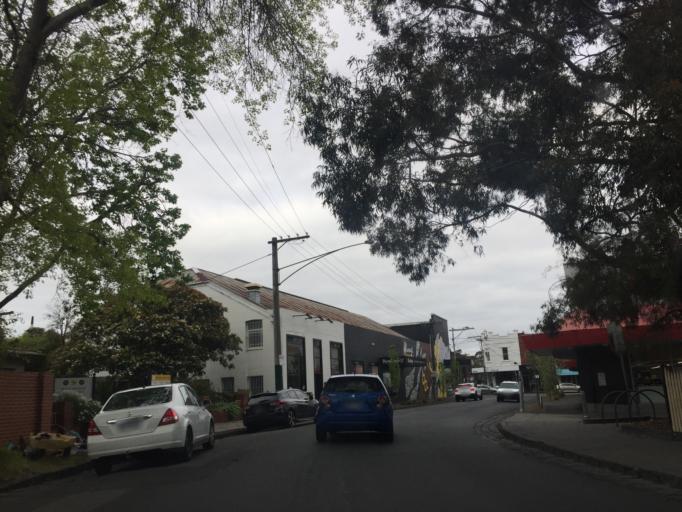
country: AU
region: Victoria
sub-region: Boroondara
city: Hawthorn East
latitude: -37.8198
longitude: 145.0348
